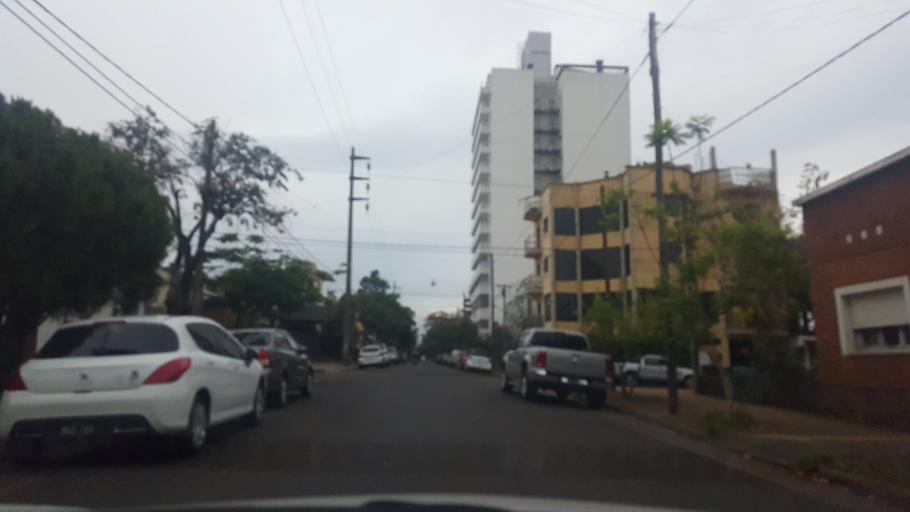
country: AR
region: Misiones
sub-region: Departamento de Capital
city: Posadas
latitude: -27.3707
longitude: -55.8888
